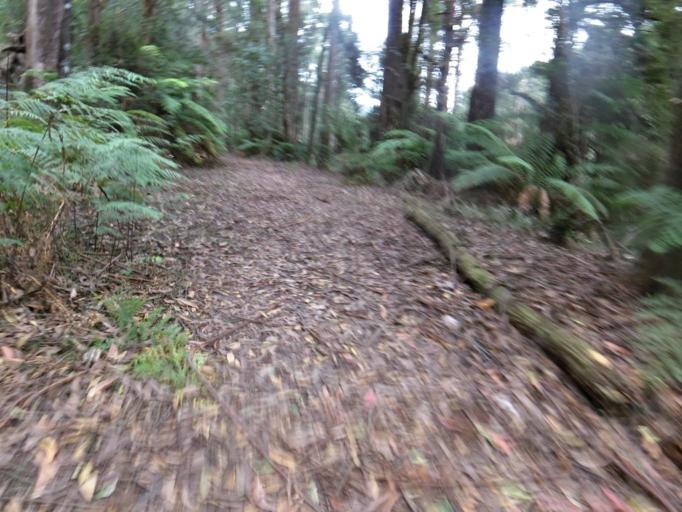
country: AU
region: Victoria
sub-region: Yarra Ranges
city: Healesville
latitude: -37.5204
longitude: 145.5208
